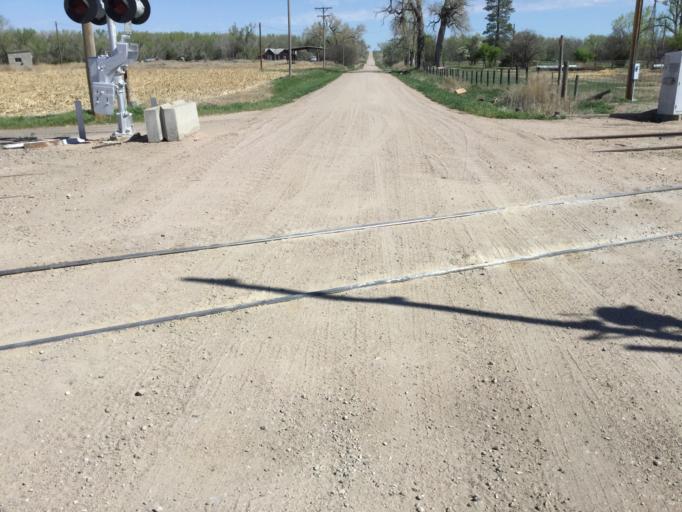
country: US
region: Kansas
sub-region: Decatur County
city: Oberlin
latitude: 39.6838
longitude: -100.2920
